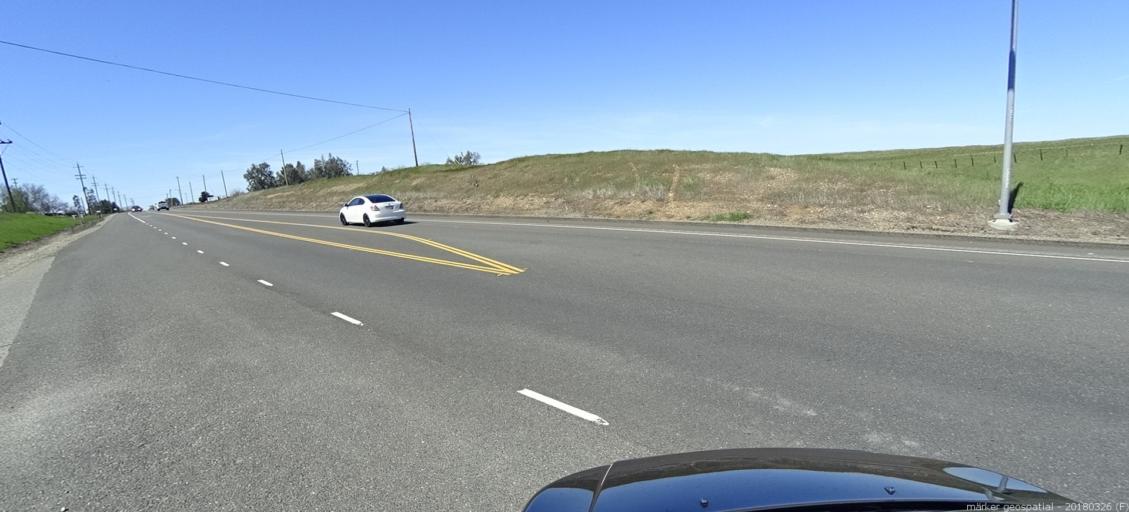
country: US
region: California
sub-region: Sacramento County
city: Wilton
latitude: 38.4984
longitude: -121.2071
